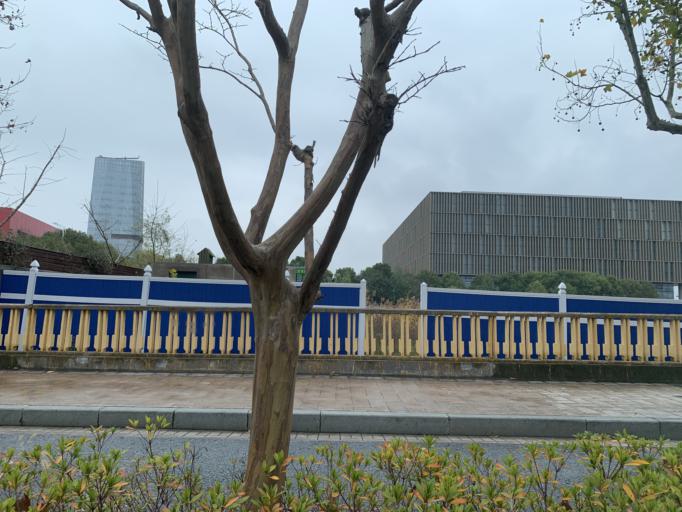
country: CN
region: Shanghai Shi
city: Huamu
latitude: 31.1943
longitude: 121.5350
